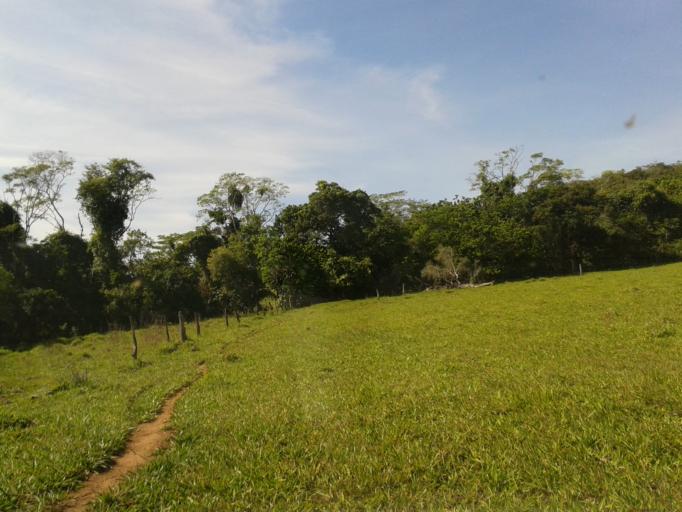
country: BR
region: Minas Gerais
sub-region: Campina Verde
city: Campina Verde
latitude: -19.4445
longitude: -49.6859
